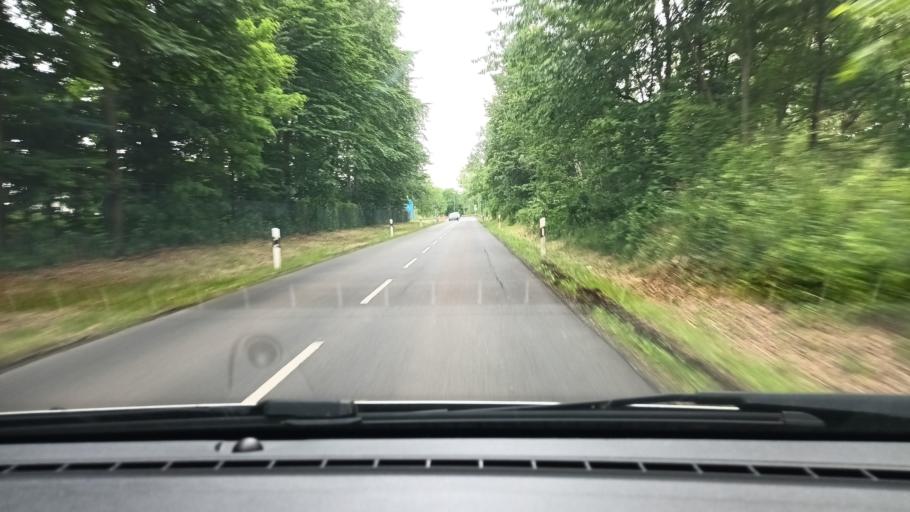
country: DE
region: North Rhine-Westphalia
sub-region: Regierungsbezirk Koln
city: Hurth
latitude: 50.8668
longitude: 6.8277
